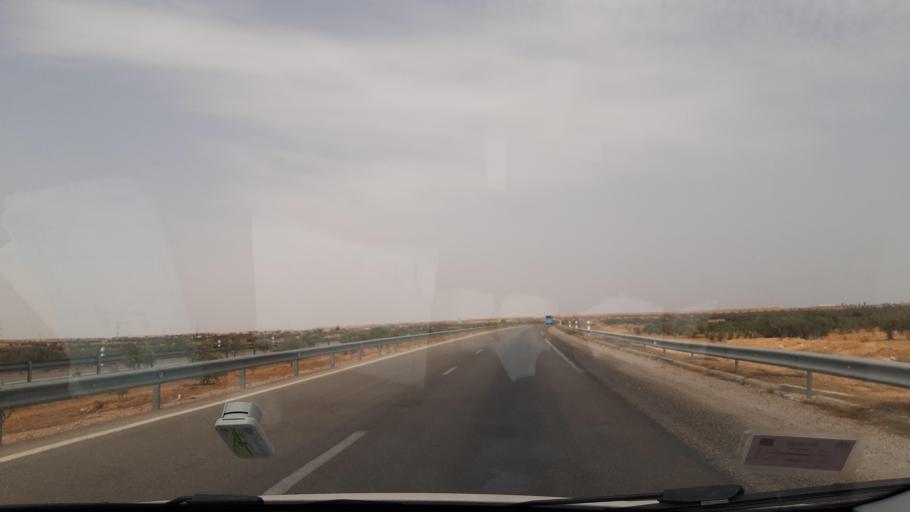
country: TN
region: Safaqis
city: Sfax
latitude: 34.7359
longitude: 10.5941
